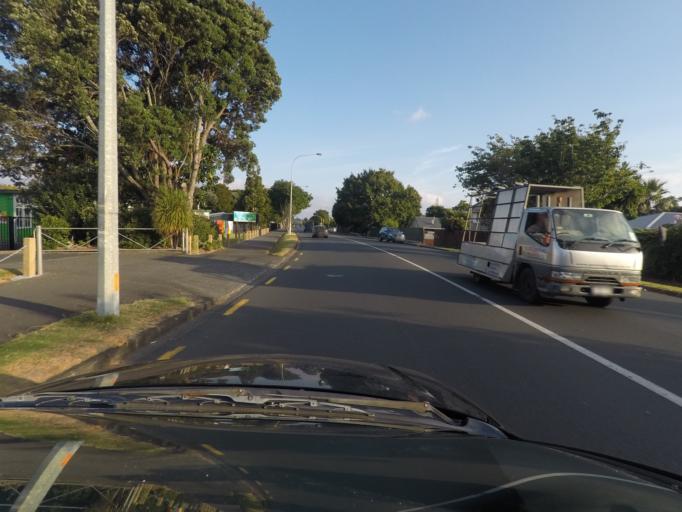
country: NZ
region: Auckland
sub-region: Auckland
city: Rosebank
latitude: -36.8890
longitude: 174.6860
